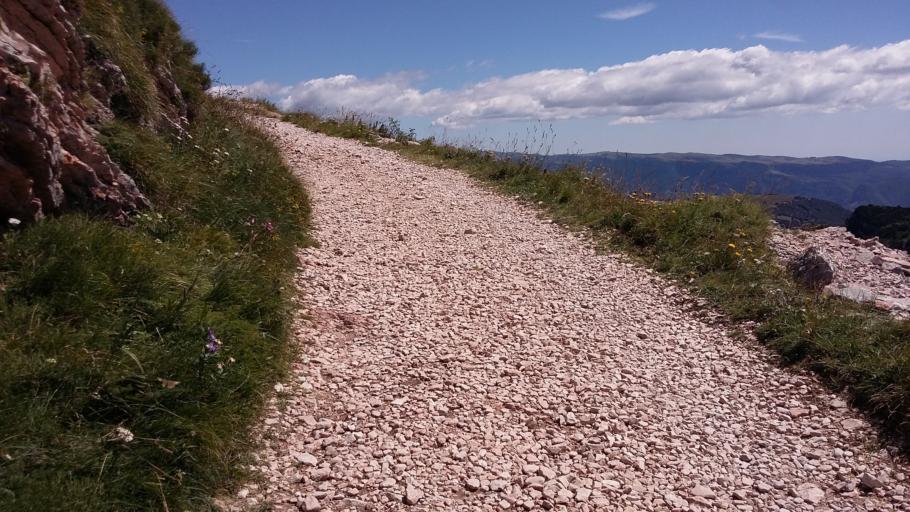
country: IT
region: Trentino-Alto Adige
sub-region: Provincia di Trento
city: Brentonico
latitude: 45.8035
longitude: 10.8912
